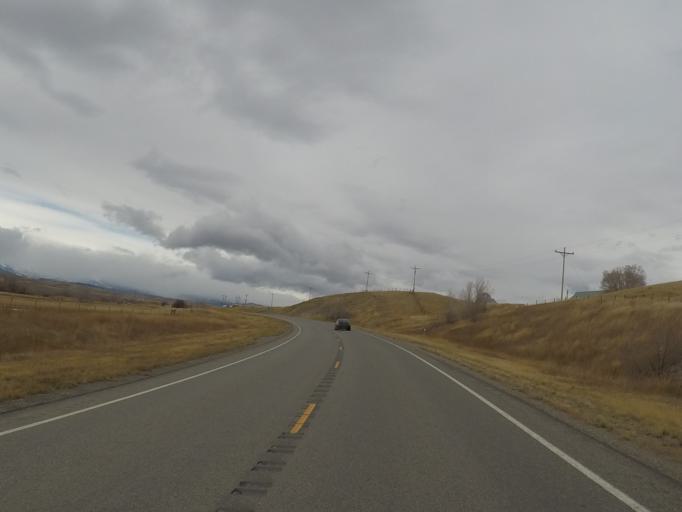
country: US
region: Montana
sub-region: Sweet Grass County
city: Big Timber
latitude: 45.8667
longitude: -109.9400
